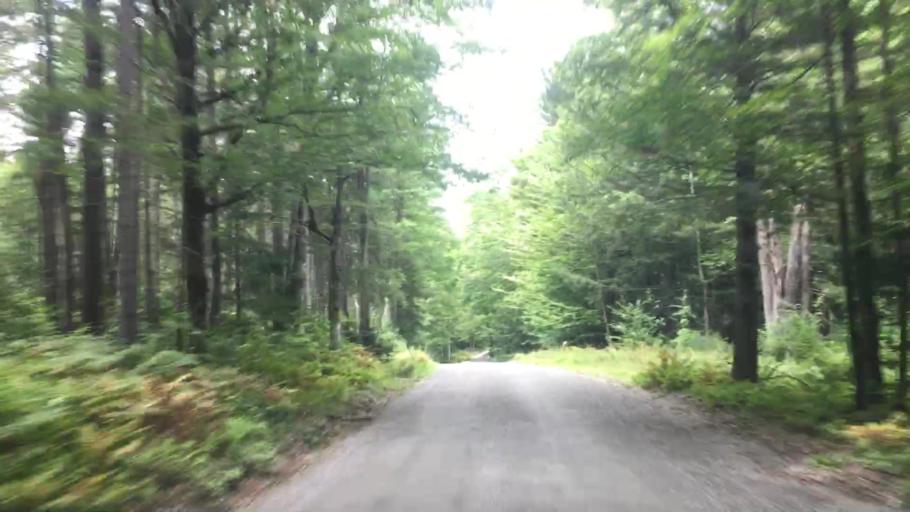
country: US
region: Vermont
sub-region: Windham County
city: Dover
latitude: 42.8294
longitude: -72.7662
